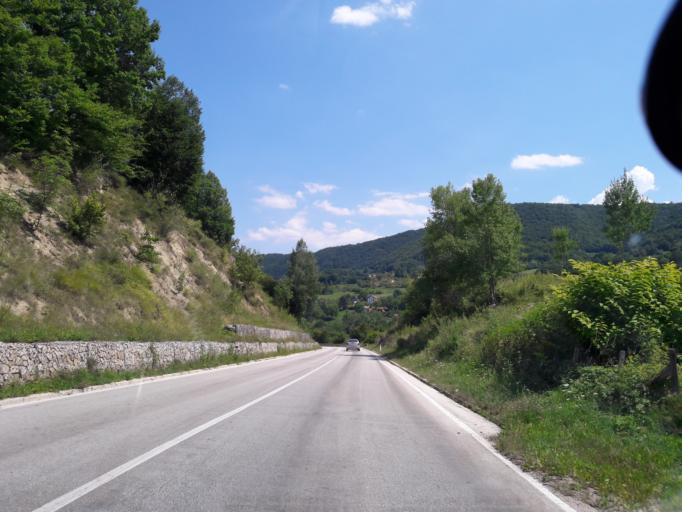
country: BA
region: Republika Srpska
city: Mrkonjic Grad
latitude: 44.4182
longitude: 17.1012
